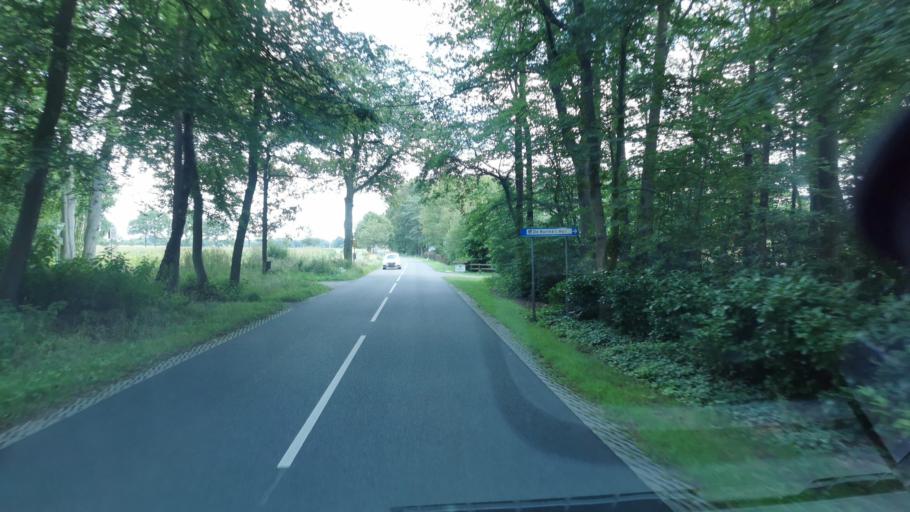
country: NL
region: Overijssel
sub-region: Gemeente Haaksbergen
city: Haaksbergen
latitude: 52.1473
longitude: 6.7974
